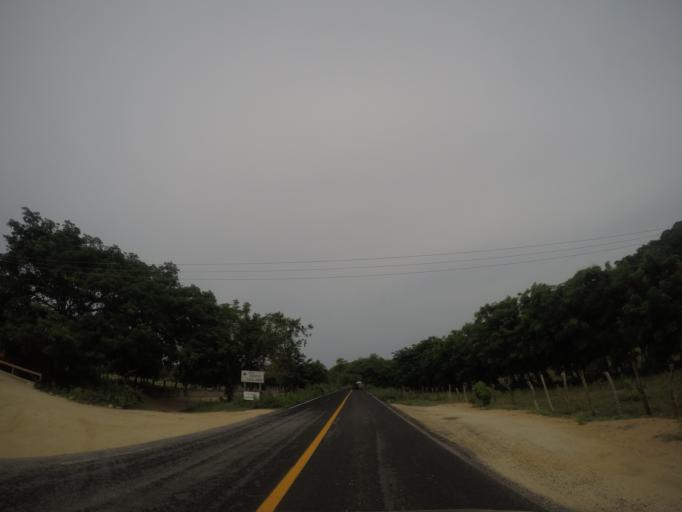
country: MX
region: Oaxaca
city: San Pedro Mixtepec
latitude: 15.9500
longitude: -97.2663
